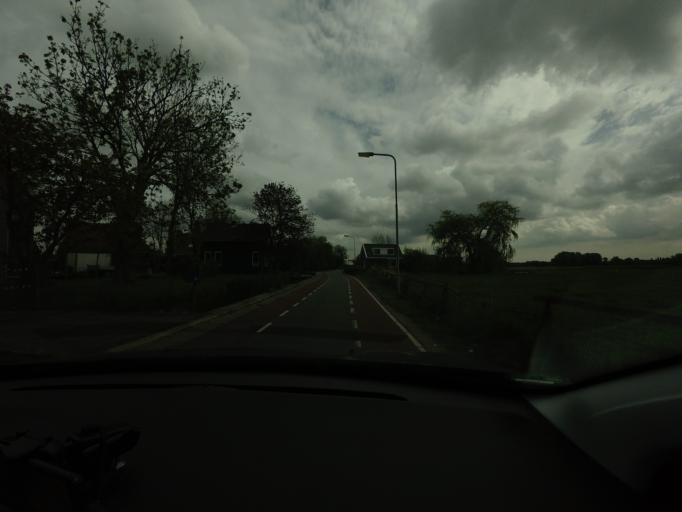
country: NL
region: North Holland
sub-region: Gemeente Landsmeer
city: Landsmeer
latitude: 52.4633
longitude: 4.8807
